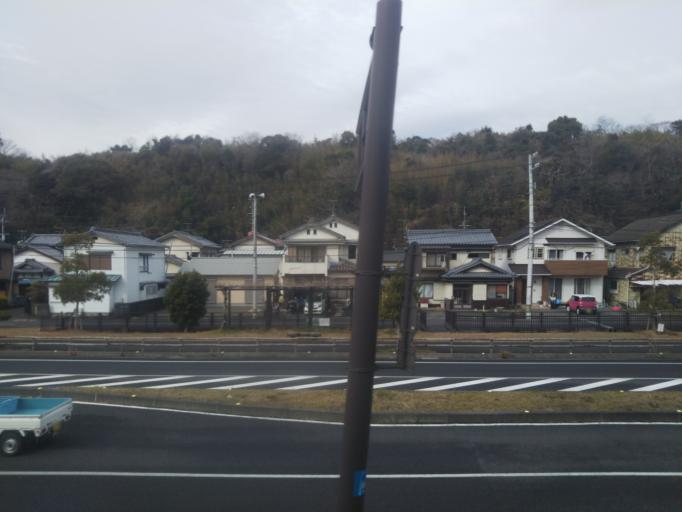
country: JP
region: Kochi
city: Nakamura
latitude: 32.9887
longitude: 132.9628
